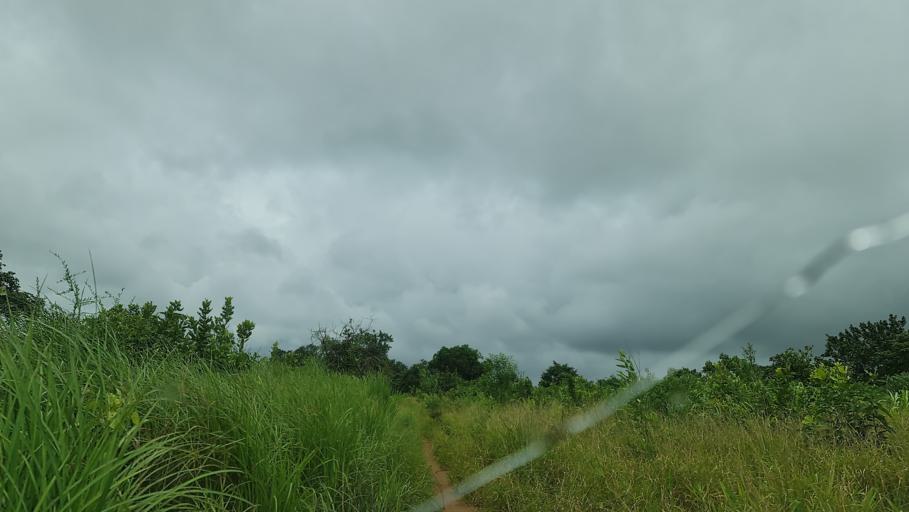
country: MW
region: Southern Region
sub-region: Nsanje District
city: Nsanje
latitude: -17.3954
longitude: 35.7860
